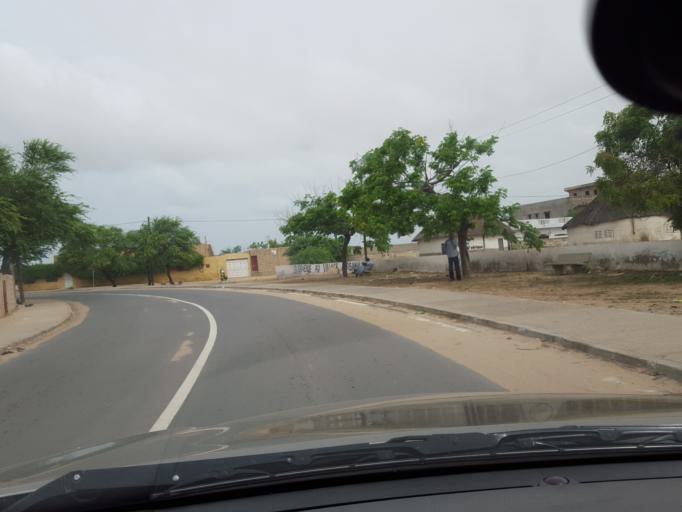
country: SN
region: Saint-Louis
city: Saint-Louis
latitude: 16.0323
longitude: -16.4889
